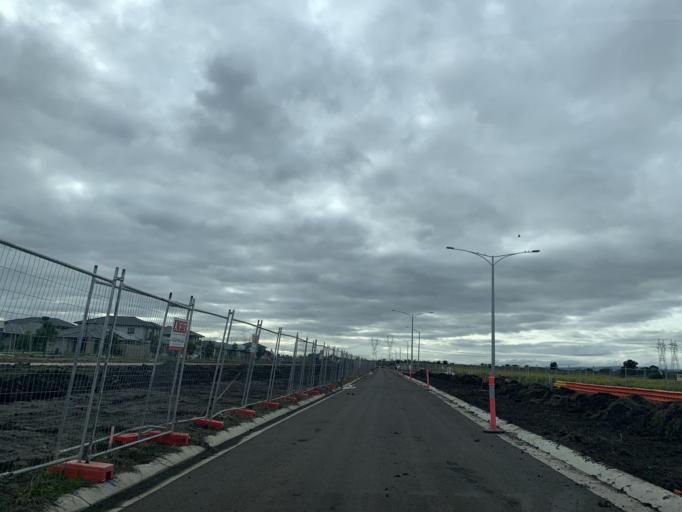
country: AU
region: Victoria
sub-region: Hume
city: Craigieburn
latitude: -37.5998
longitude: 145.0002
